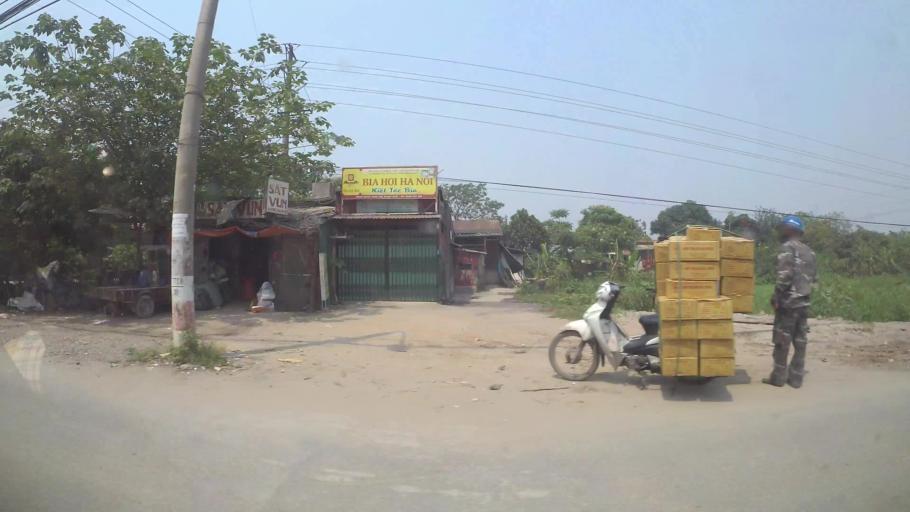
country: VN
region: Ha Noi
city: Van Dien
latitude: 20.9509
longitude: 105.8198
